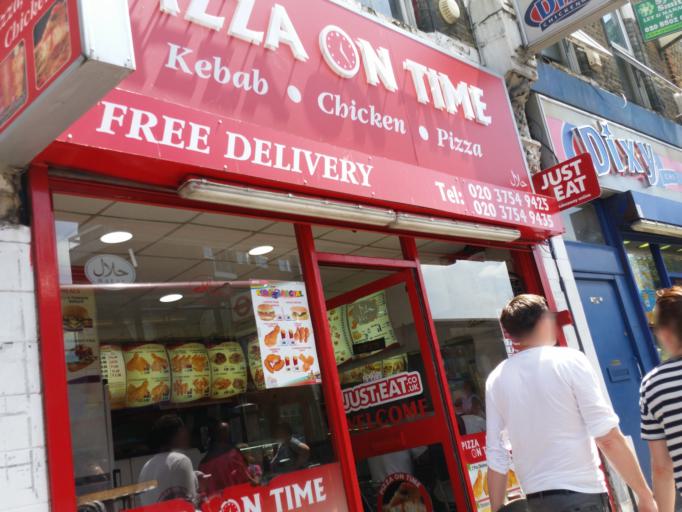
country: GB
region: England
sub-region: Greater London
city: Harringay
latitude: 51.5745
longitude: -0.0723
